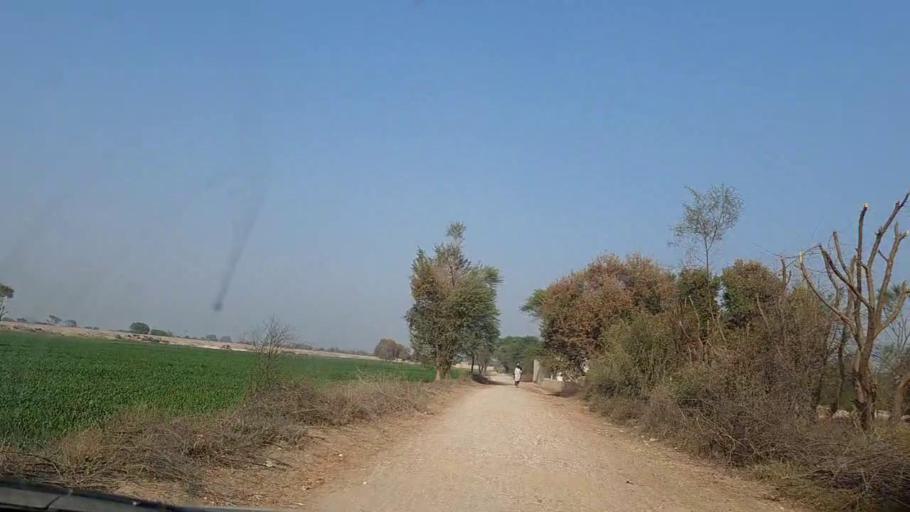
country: PK
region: Sindh
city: Moro
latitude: 26.7966
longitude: 67.9437
